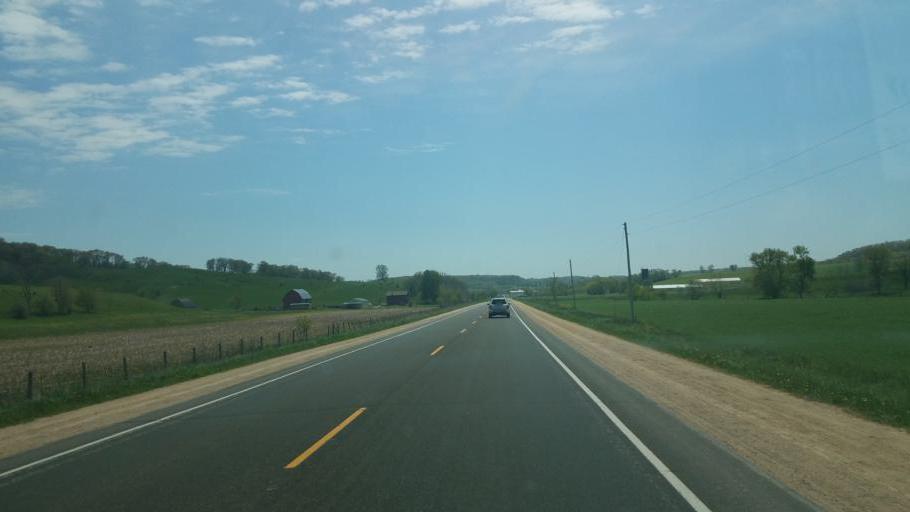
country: US
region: Wisconsin
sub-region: Monroe County
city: Tomah
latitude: 43.8560
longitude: -90.4737
